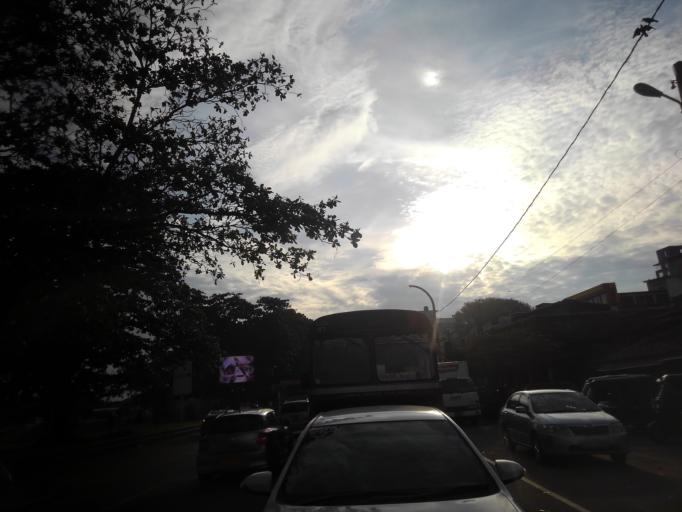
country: LK
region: Southern
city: Galle
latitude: 6.0342
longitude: 80.2189
